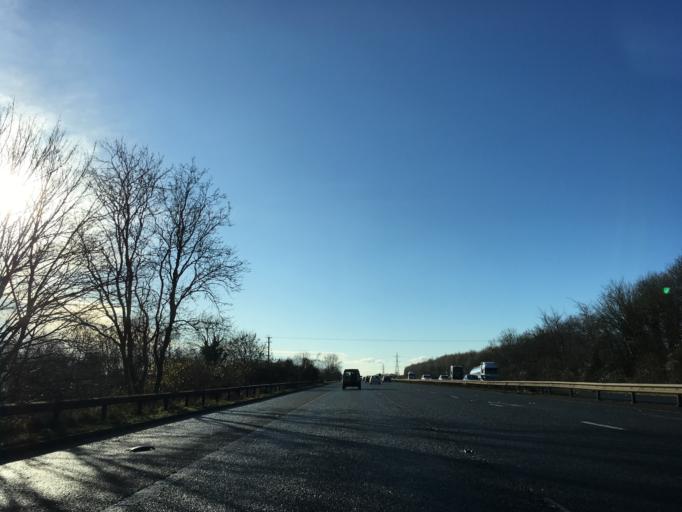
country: GB
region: England
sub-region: South Gloucestershire
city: Tytherington
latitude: 51.5955
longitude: -2.4872
